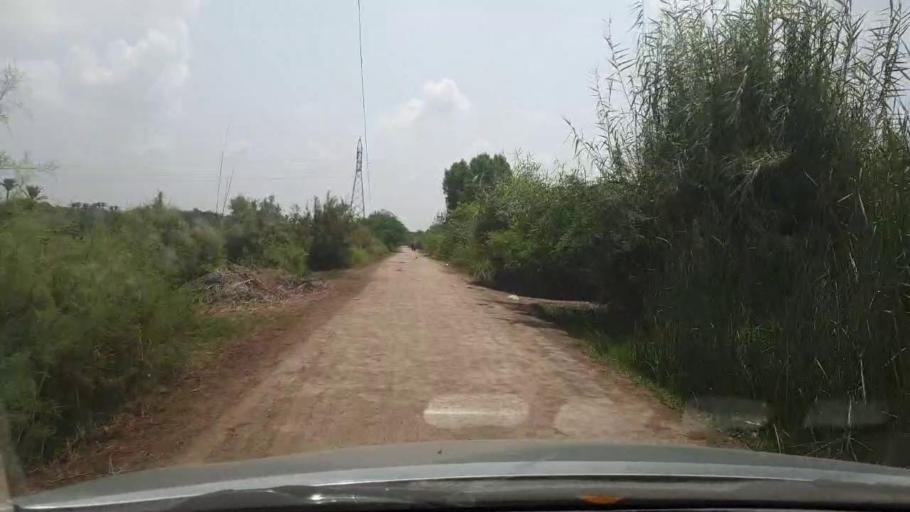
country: PK
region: Sindh
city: Khairpur
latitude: 27.4866
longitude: 68.7253
